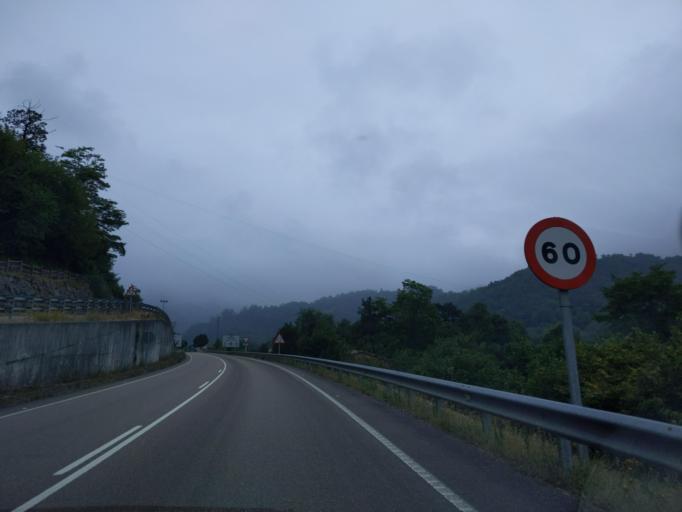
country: ES
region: Asturias
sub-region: Province of Asturias
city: Pola de Laviana
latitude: 43.2348
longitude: -5.5373
